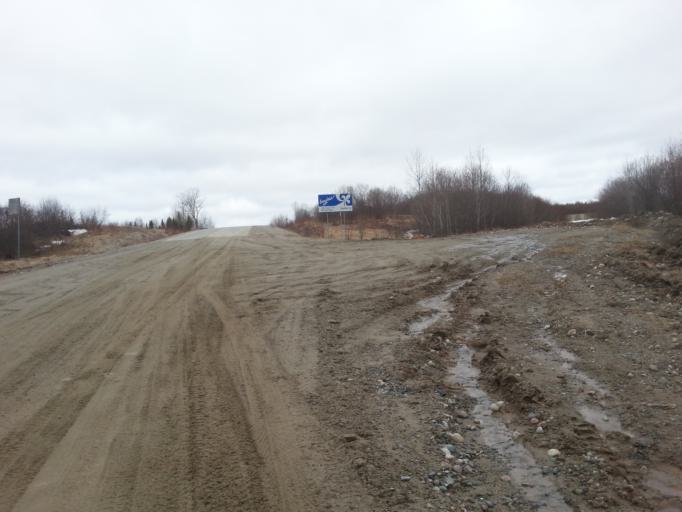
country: CA
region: Quebec
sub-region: Abitibi-Temiscamingue
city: La Sarre
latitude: 48.9519
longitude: -79.5183
